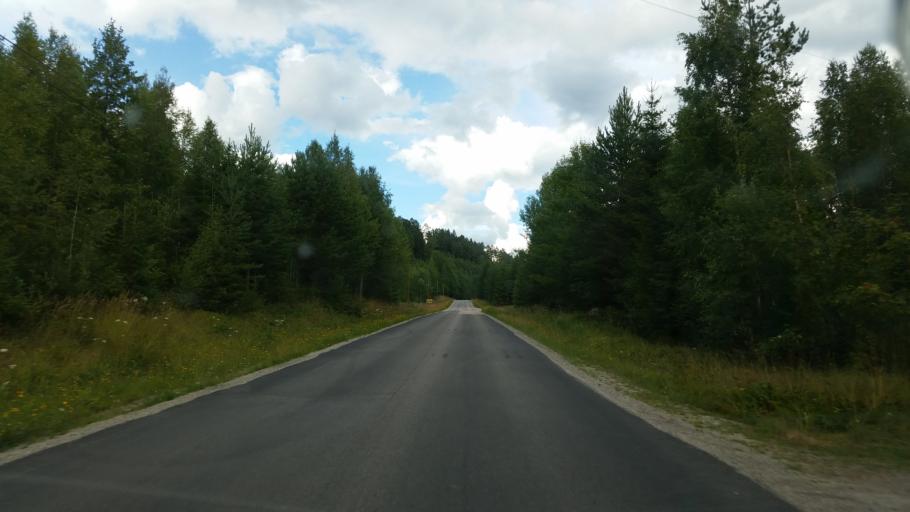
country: SE
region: Gaevleborg
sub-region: Hudiksvalls Kommun
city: Delsbo
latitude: 61.9095
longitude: 16.5713
